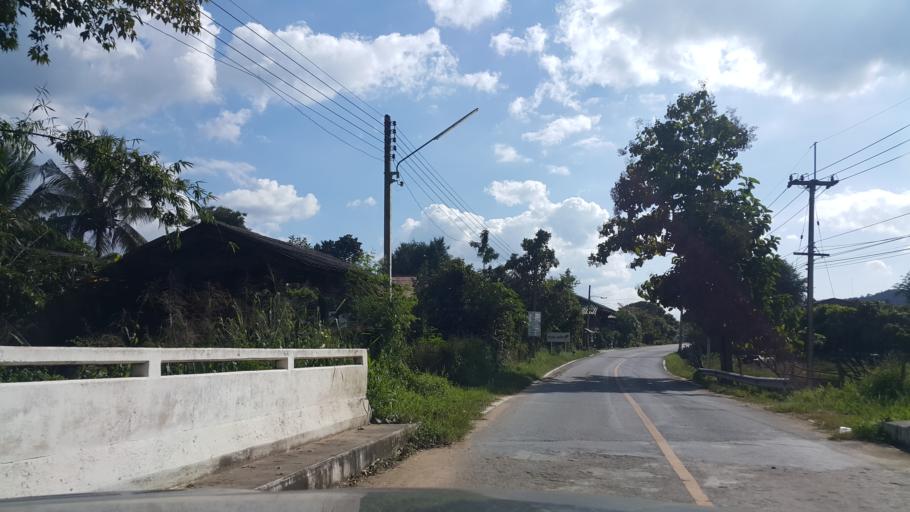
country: TH
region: Lamphun
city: Ban Thi
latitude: 18.5895
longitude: 99.2658
